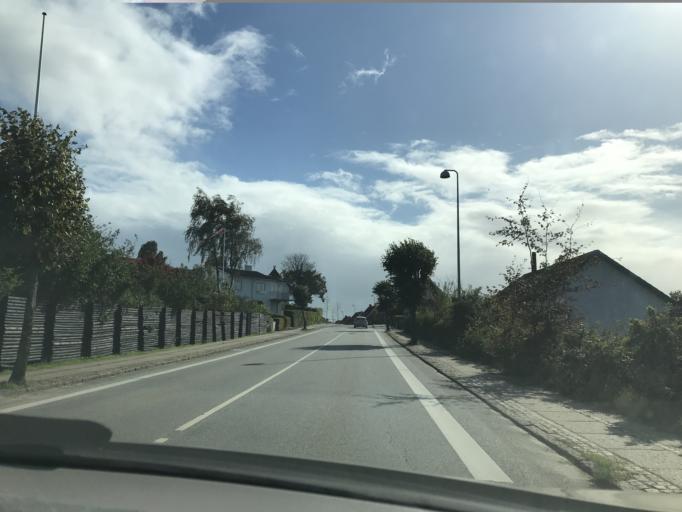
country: DK
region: Central Jutland
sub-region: Skanderborg Kommune
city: Skanderborg
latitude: 56.0373
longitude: 9.9193
